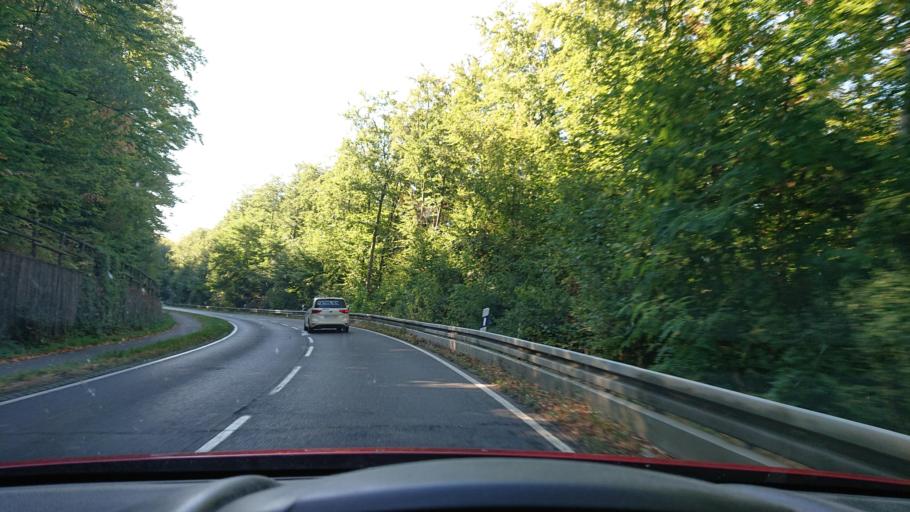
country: DE
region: North Rhine-Westphalia
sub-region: Regierungsbezirk Koln
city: Bergheim
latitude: 50.9465
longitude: 6.6924
